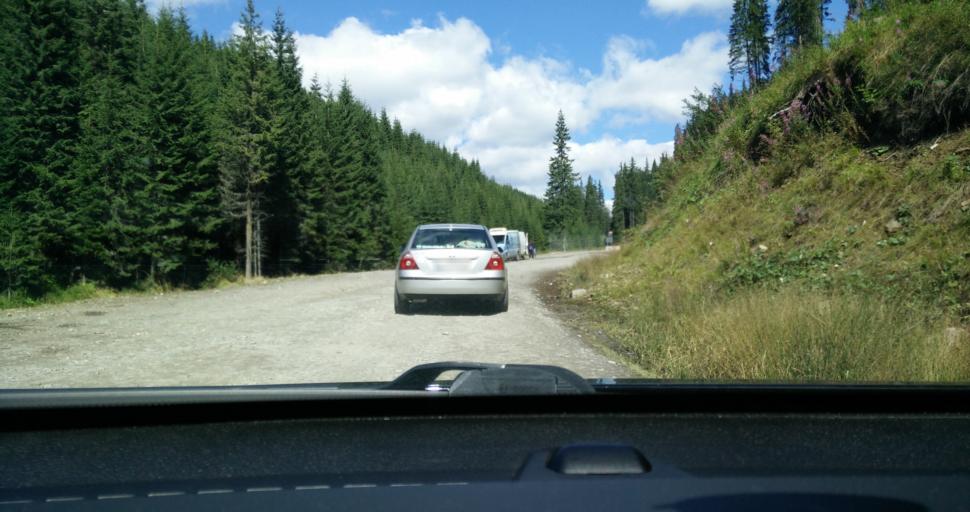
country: RO
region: Hunedoara
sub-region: Oras Petrila
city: Petrila
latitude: 45.4388
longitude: 23.6291
